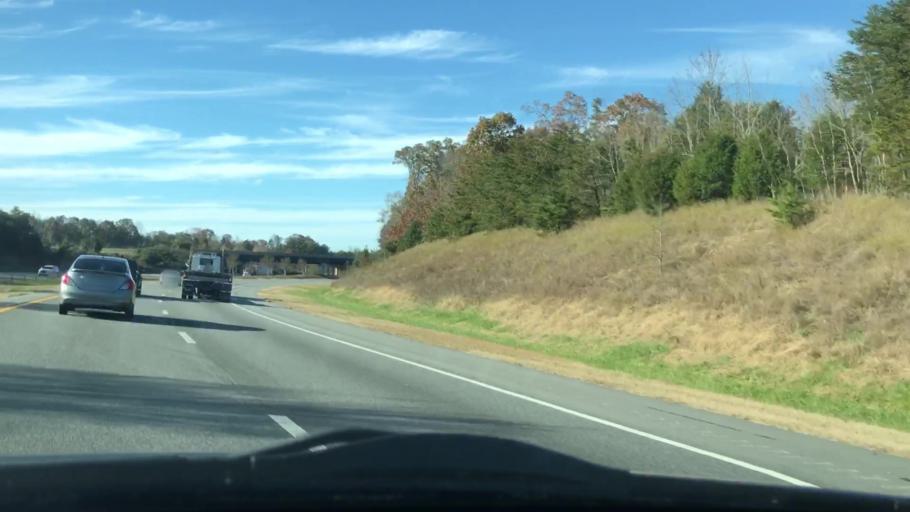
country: US
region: North Carolina
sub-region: Guilford County
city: High Point
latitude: 36.0077
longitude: -80.0317
